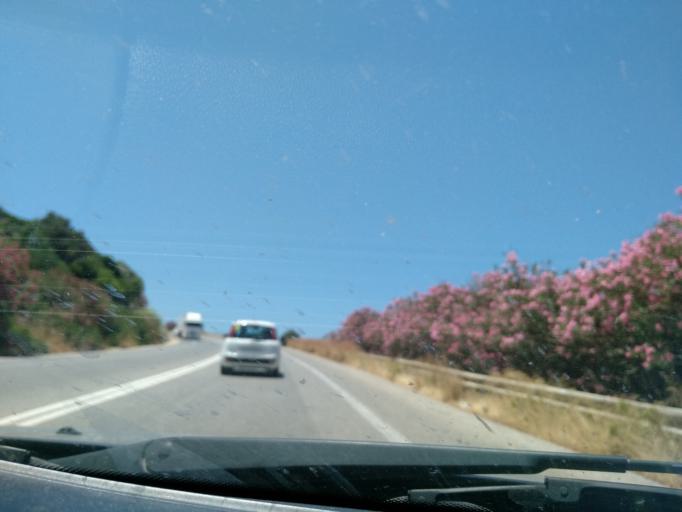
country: GR
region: Crete
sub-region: Nomos Rethymnis
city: Perama
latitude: 35.4090
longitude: 24.8103
